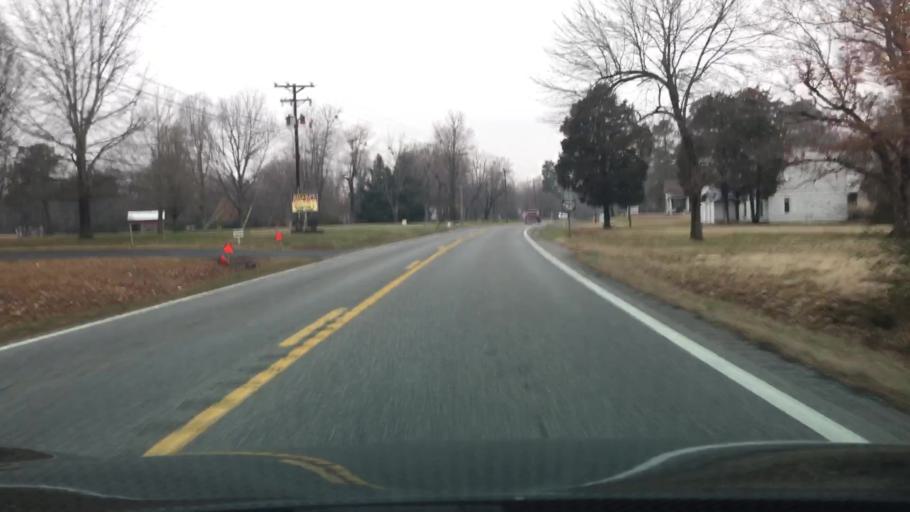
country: US
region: Kentucky
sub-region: Livingston County
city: Ledbetter
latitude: 36.9682
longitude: -88.4562
